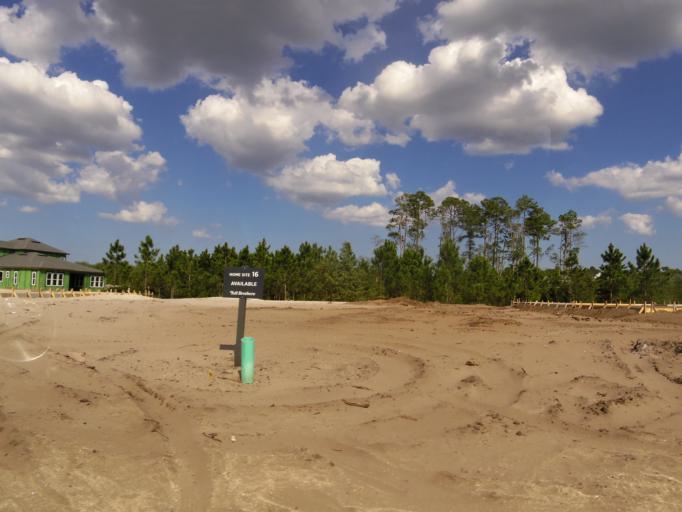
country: US
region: Florida
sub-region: Saint Johns County
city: Palm Valley
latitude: 30.1902
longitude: -81.5030
